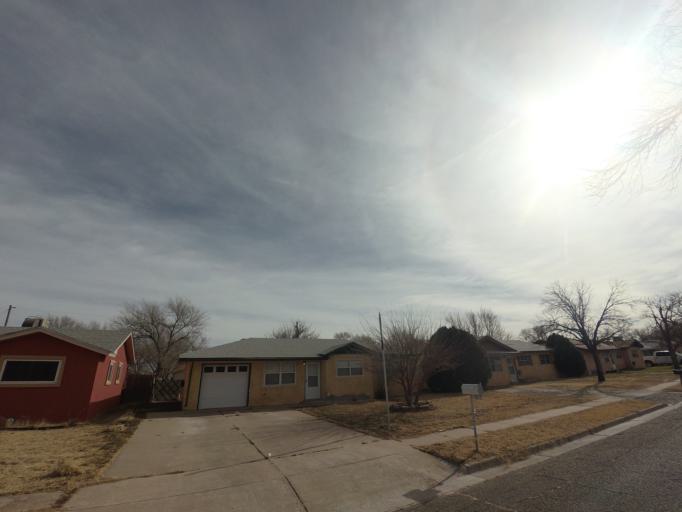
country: US
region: New Mexico
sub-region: Curry County
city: Clovis
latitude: 34.4114
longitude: -103.2394
